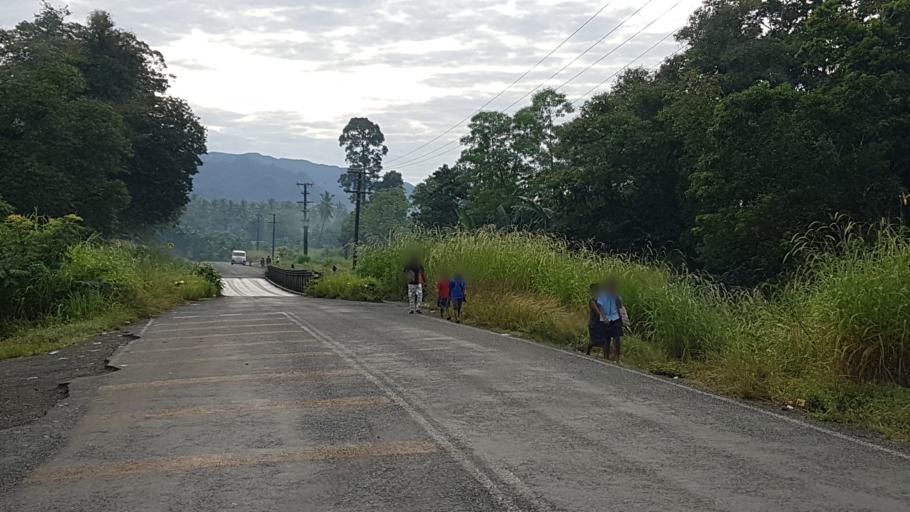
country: PG
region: Milne Bay
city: Alotau
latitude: -10.3162
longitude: 150.4676
